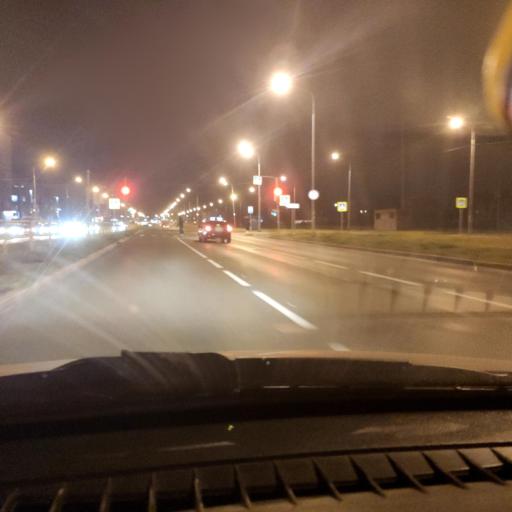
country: RU
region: Samara
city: Tol'yatti
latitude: 53.5410
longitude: 49.3637
